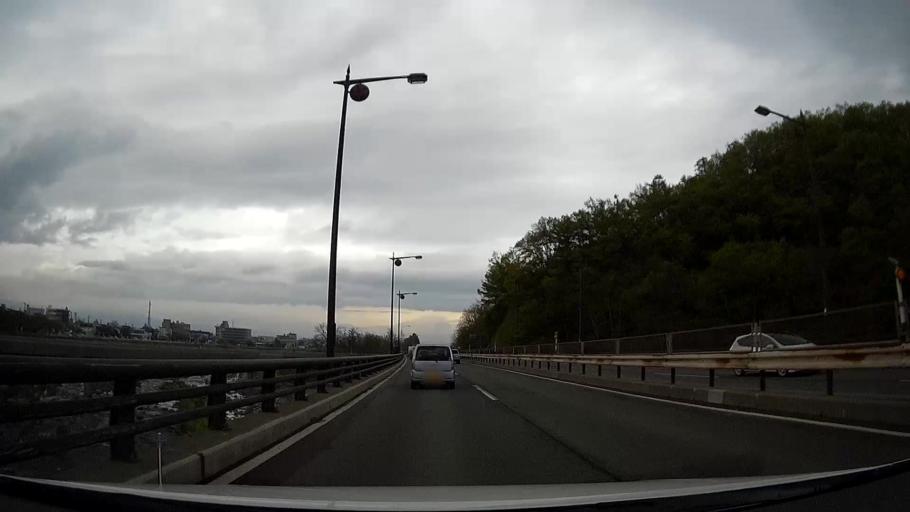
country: JP
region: Yamagata
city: Yamagata-shi
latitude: 38.2499
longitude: 140.3561
